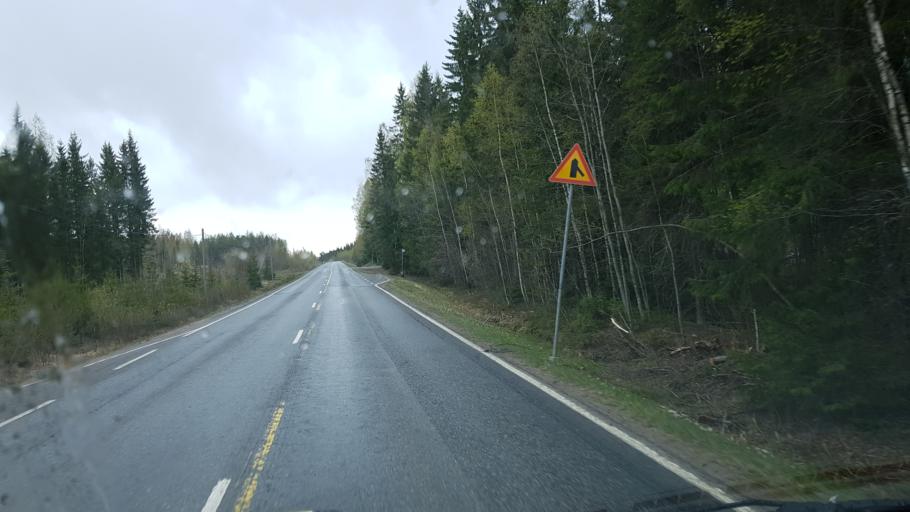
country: FI
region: Pirkanmaa
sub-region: Tampere
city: Pirkkala
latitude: 61.4008
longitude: 23.6300
